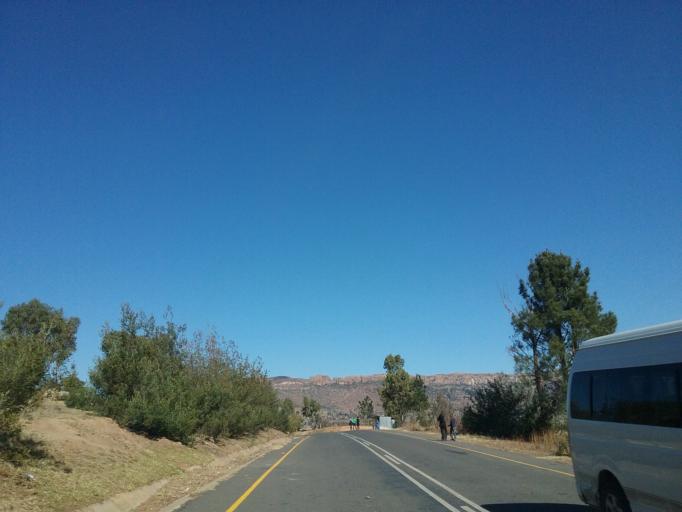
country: LS
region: Maseru
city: Nako
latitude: -29.4947
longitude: 27.6405
